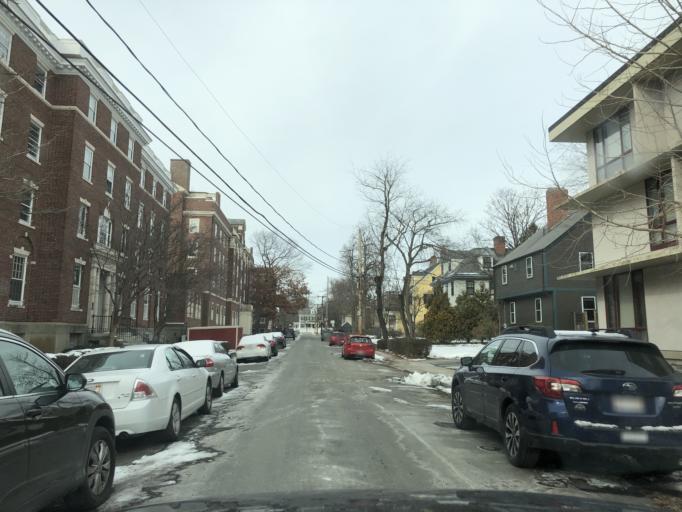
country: US
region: Massachusetts
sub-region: Middlesex County
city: Cambridge
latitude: 42.3813
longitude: -71.1232
